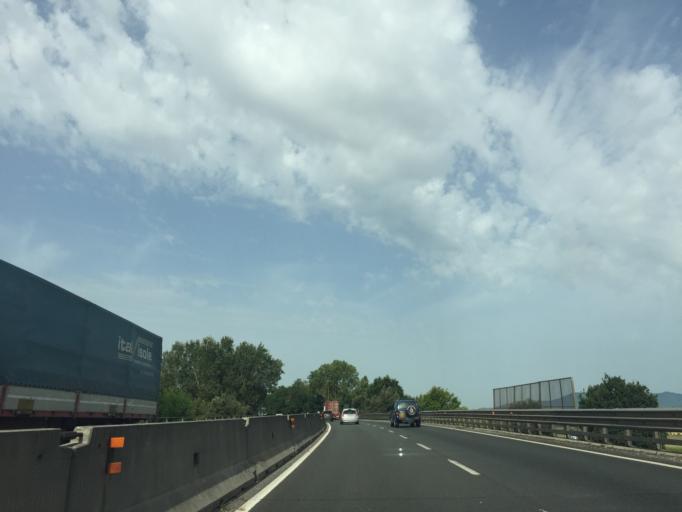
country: IT
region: Tuscany
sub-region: Province of Pisa
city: Marti
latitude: 43.6719
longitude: 10.7261
